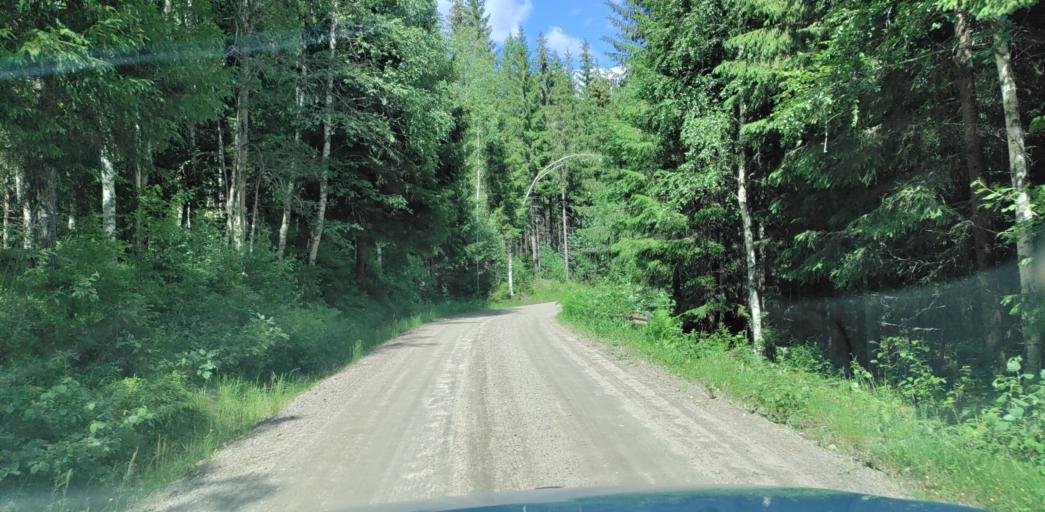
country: SE
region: Vaermland
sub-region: Sunne Kommun
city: Sunne
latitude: 60.0471
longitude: 13.2570
